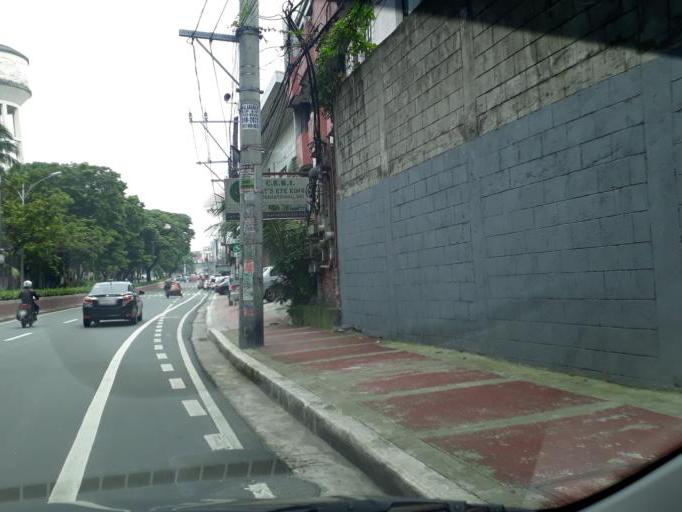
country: PH
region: Metro Manila
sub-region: Quezon City
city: Quezon City
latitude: 14.6340
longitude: 121.0544
